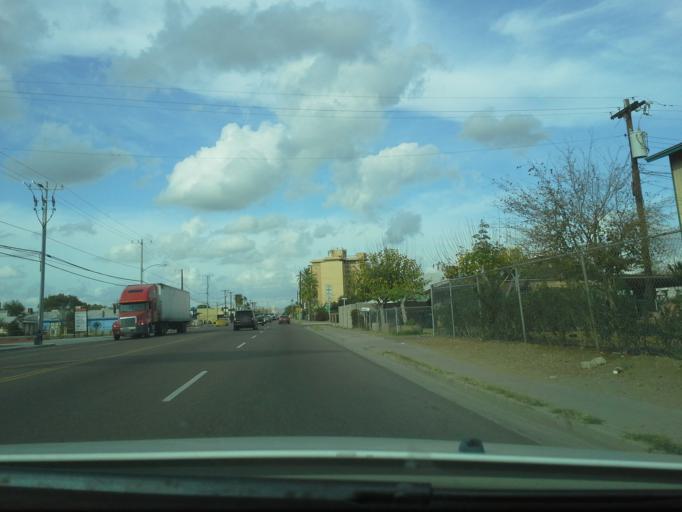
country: US
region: Arizona
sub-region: Maricopa County
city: Phoenix
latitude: 33.4303
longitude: -112.0824
